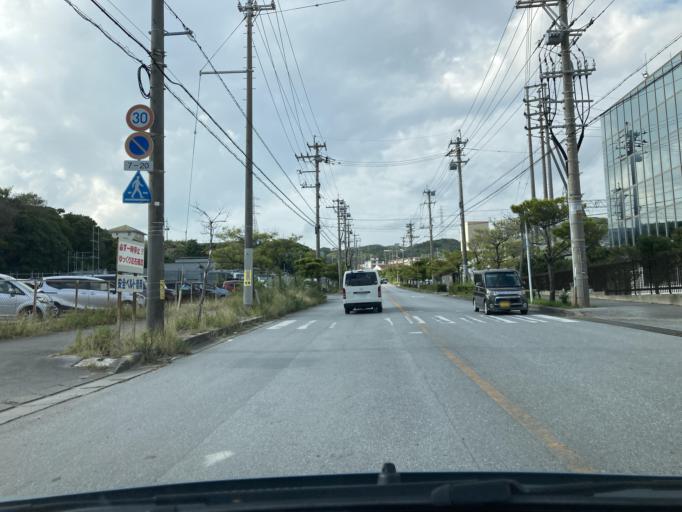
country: JP
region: Okinawa
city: Ginowan
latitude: 26.2310
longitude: 127.7732
